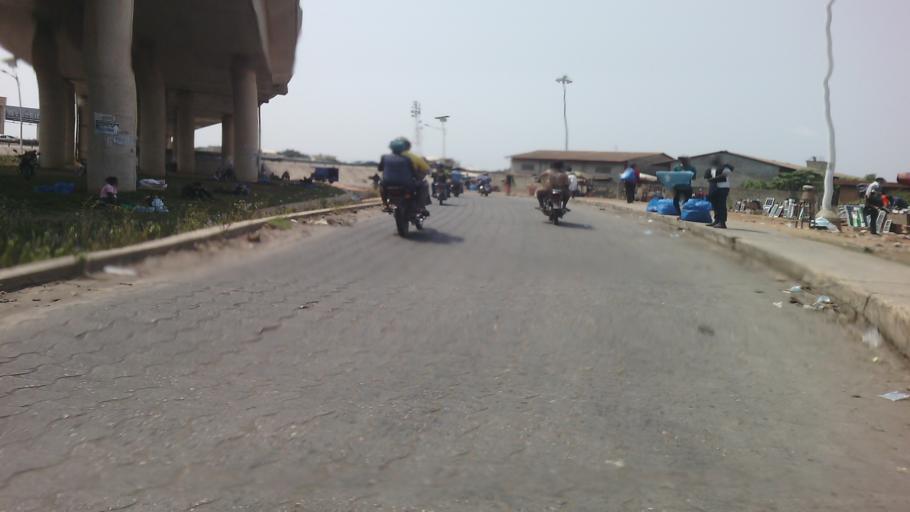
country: BJ
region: Atlantique
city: Abomey-Calavi
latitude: 6.3906
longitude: 2.3539
